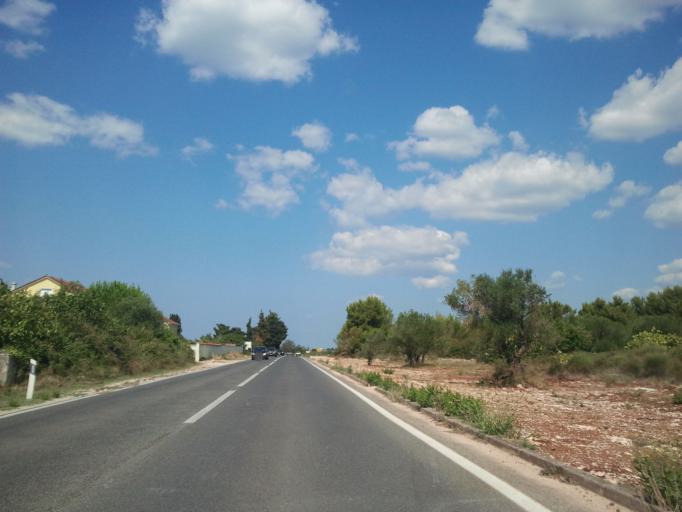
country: HR
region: Zadarska
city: Turanj
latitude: 43.9768
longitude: 15.3974
